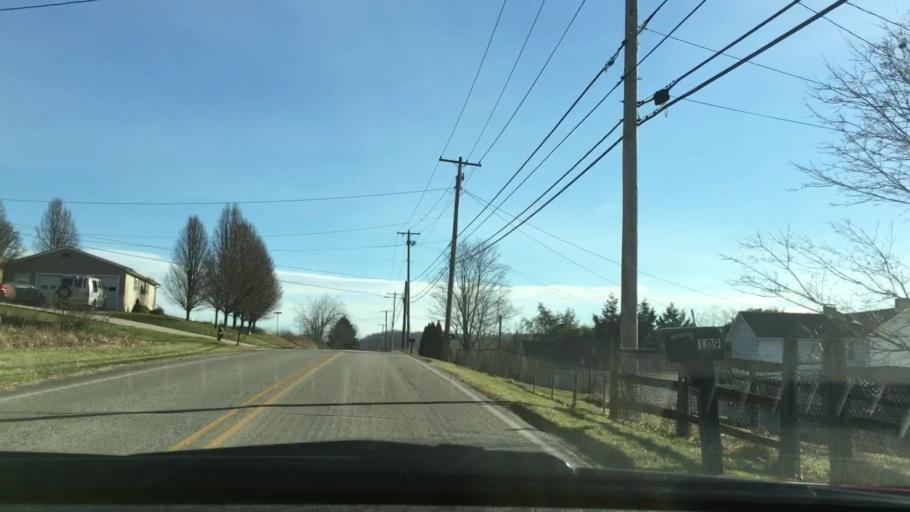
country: US
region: Pennsylvania
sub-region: Westmoreland County
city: Irwin
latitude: 40.2653
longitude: -79.6903
